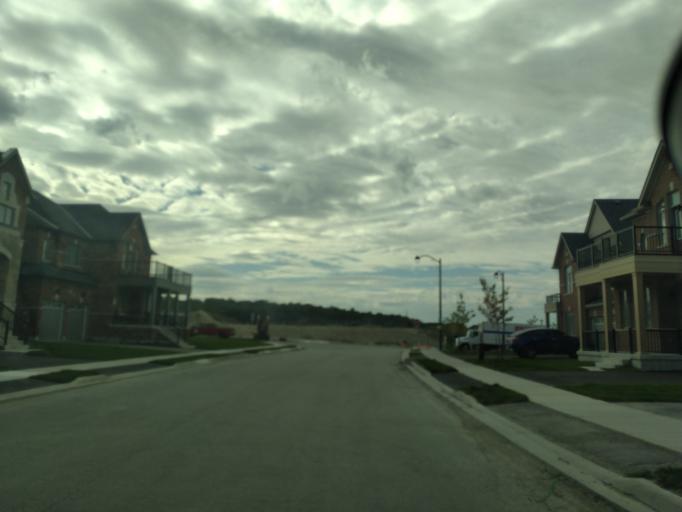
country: CA
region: Ontario
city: Newmarket
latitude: 44.0953
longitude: -79.5013
